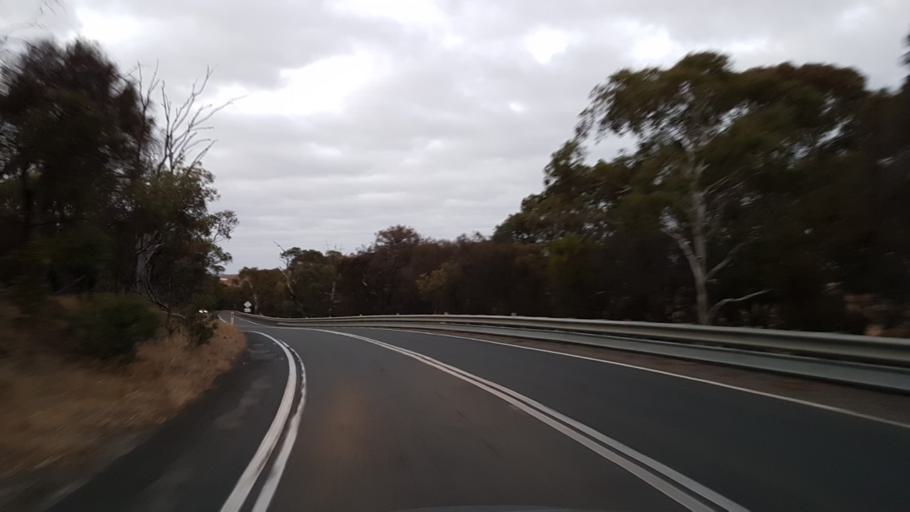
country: AU
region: South Australia
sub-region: Mount Barker
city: Callington
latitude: -35.0499
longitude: 139.0007
